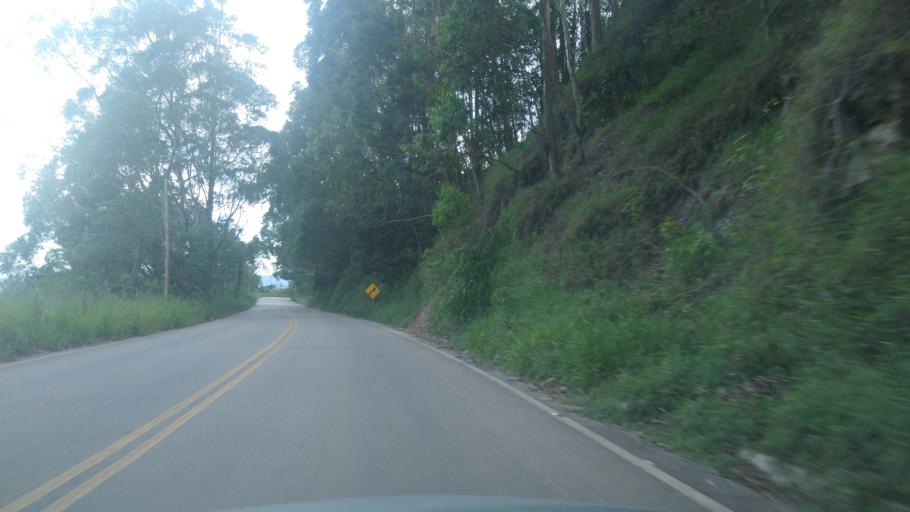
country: BR
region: Minas Gerais
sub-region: Extrema
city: Extrema
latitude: -22.7630
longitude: -46.3296
